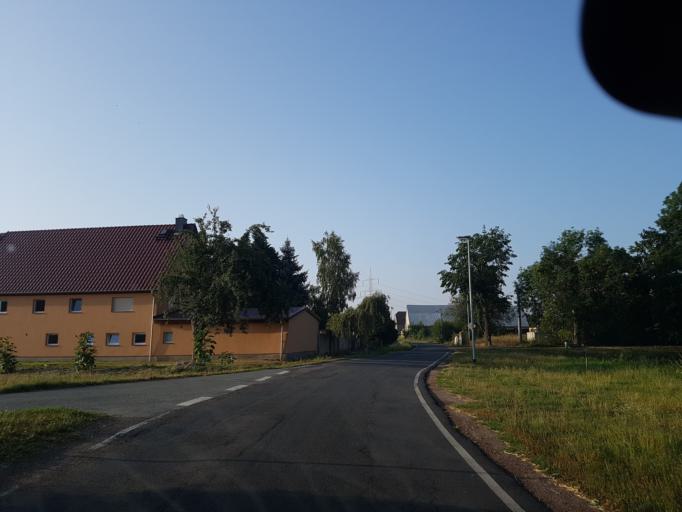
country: DE
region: Saxony
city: Strehla
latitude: 51.3104
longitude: 13.1945
